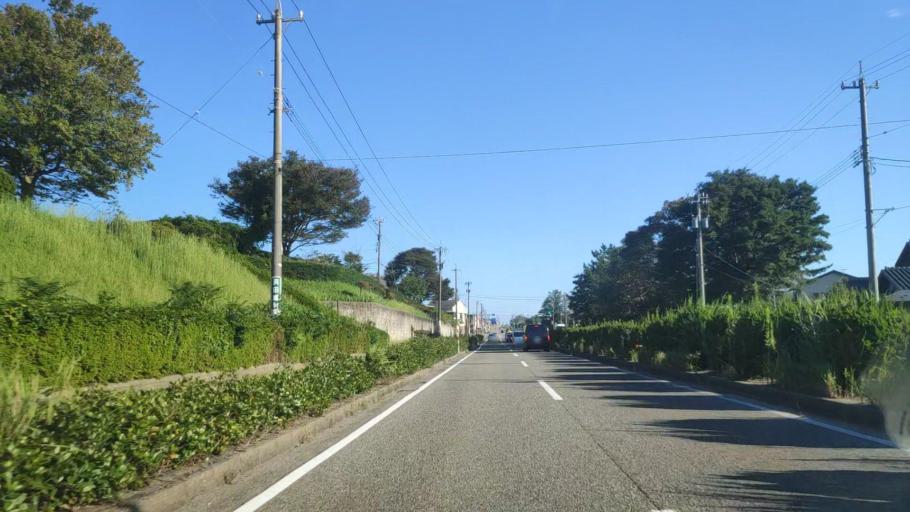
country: JP
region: Ishikawa
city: Tsubata
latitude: 36.7182
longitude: 136.6980
